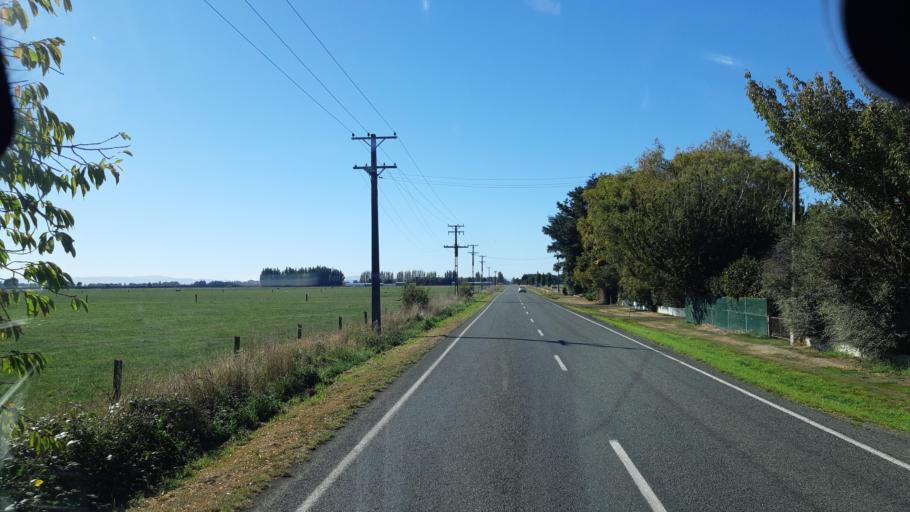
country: NZ
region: Southland
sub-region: Southland District
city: Winton
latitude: -46.1490
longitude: 168.1518
